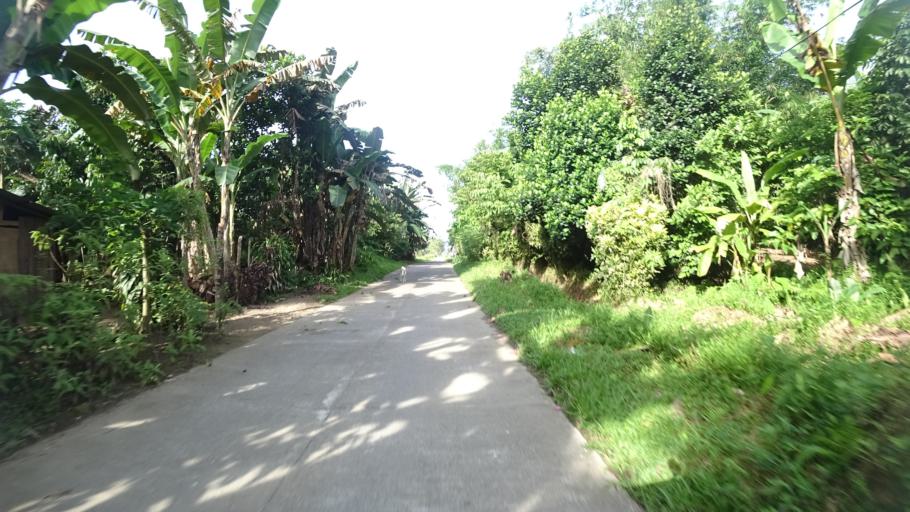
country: PH
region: Eastern Visayas
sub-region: Province of Leyte
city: Pastrana
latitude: 11.1583
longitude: 124.8628
